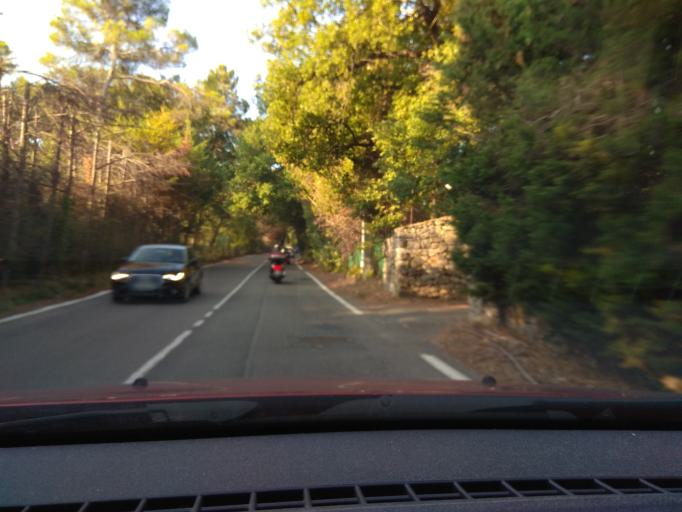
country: FR
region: Provence-Alpes-Cote d'Azur
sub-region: Departement des Alpes-Maritimes
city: Valbonne
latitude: 43.6465
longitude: 7.0218
